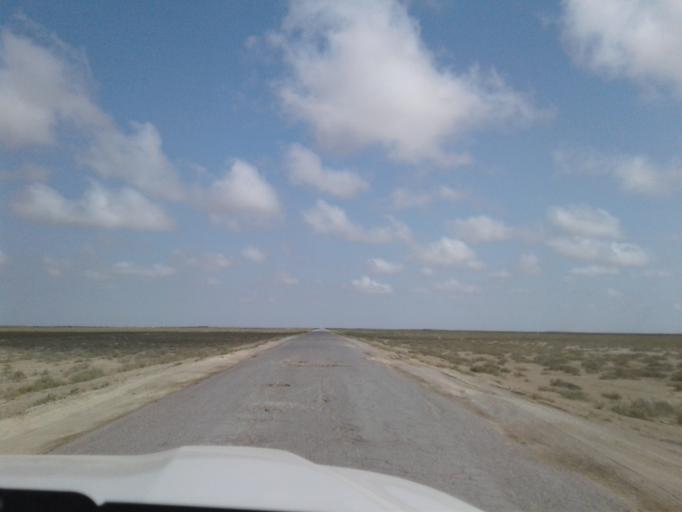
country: IR
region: Golestan
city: Gomishan
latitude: 37.6131
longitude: 53.9262
